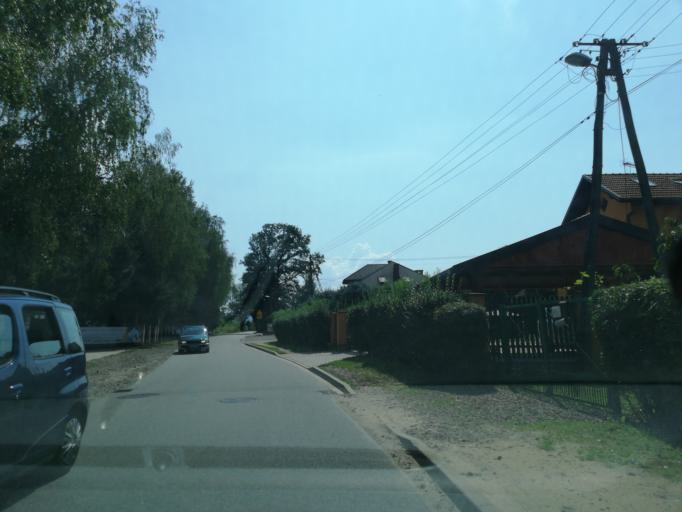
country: PL
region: Lesser Poland Voivodeship
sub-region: Powiat nowosadecki
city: Chelmiec
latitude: 49.6372
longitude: 20.6794
